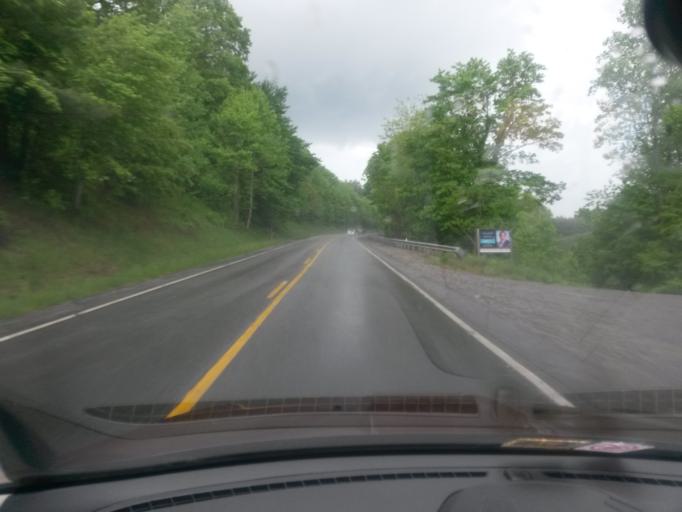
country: US
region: Virginia
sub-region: Floyd County
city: Floyd
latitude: 36.9678
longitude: -80.3803
